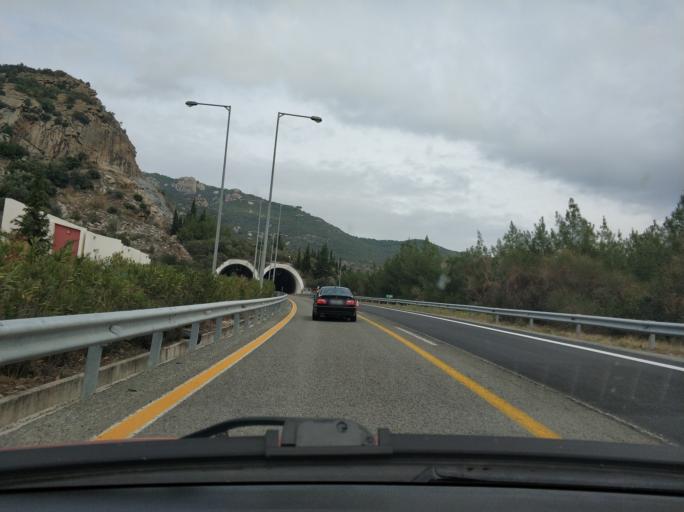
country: GR
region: East Macedonia and Thrace
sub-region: Nomos Kavalas
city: Palaio Tsifliki
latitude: 40.9045
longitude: 24.3409
